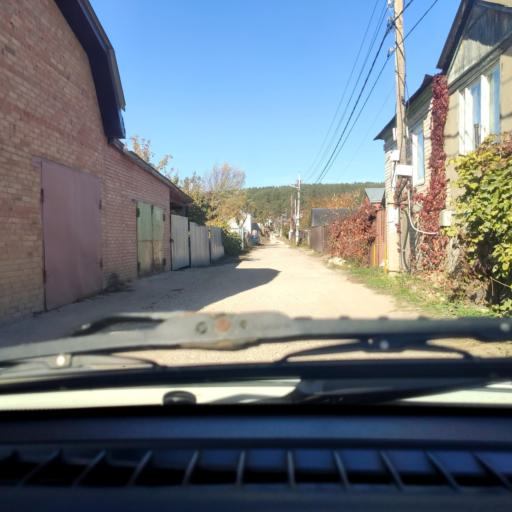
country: RU
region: Samara
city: Zhigulevsk
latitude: 53.4659
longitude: 49.5883
